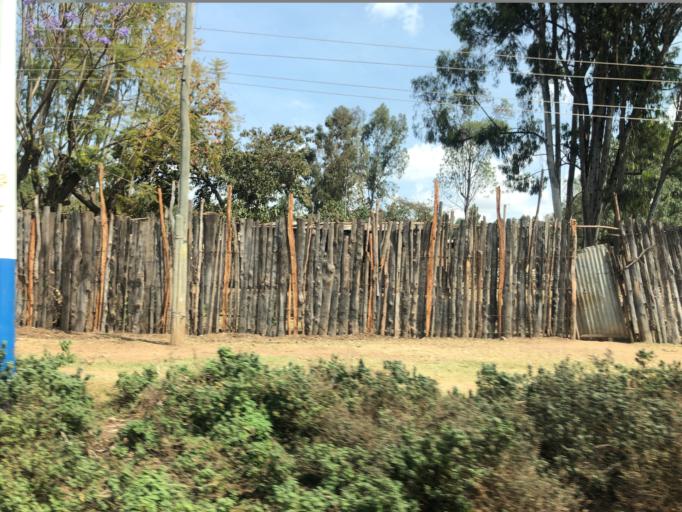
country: ET
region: Oromiya
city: Shashemene
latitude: 7.2728
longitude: 38.6551
